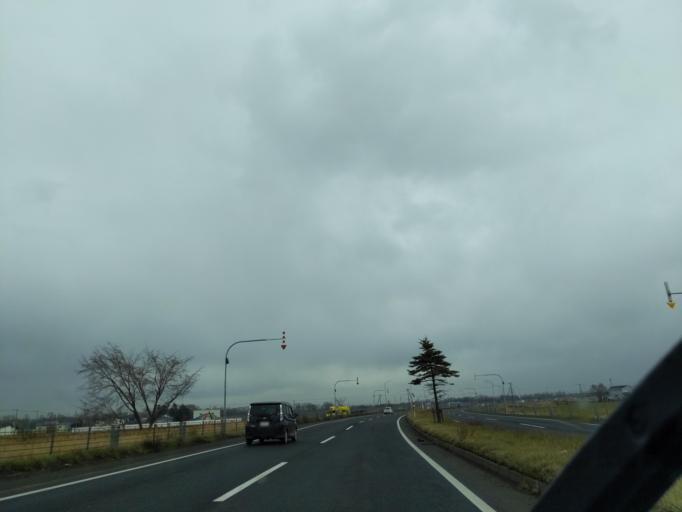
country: JP
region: Hokkaido
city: Ishikari
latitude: 43.1817
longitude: 141.3757
